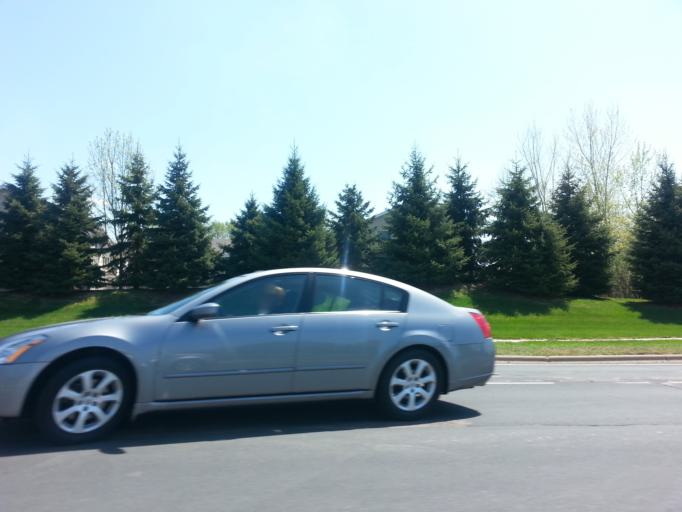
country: US
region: Minnesota
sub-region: Scott County
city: Savage
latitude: 44.7530
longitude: -93.3164
